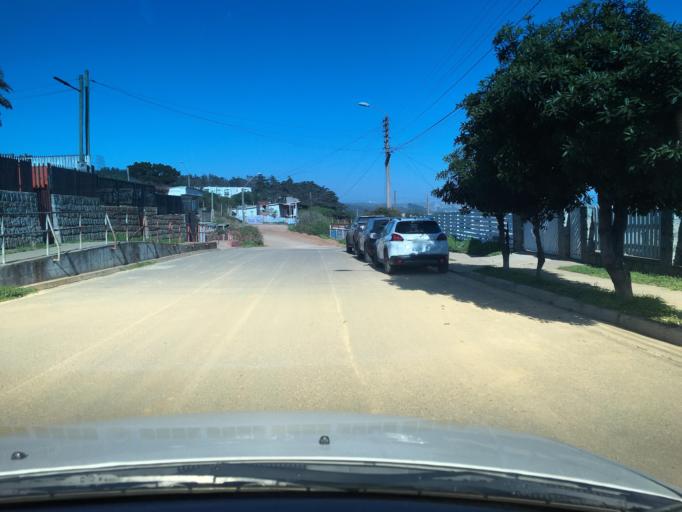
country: CL
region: Valparaiso
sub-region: San Antonio Province
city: El Tabo
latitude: -33.4574
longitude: -71.6588
